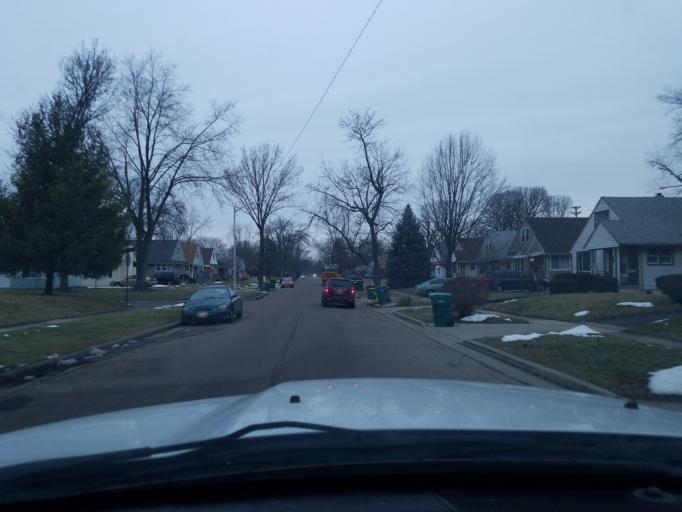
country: US
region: Ohio
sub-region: Montgomery County
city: Oakwood
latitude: 39.7107
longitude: -84.1534
